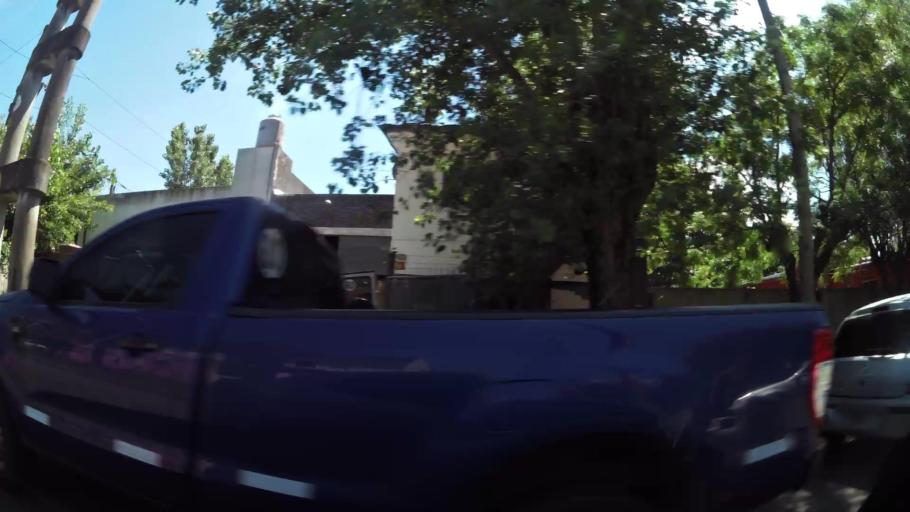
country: AR
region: Buenos Aires
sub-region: Partido de Tigre
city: Tigre
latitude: -34.4330
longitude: -58.5832
